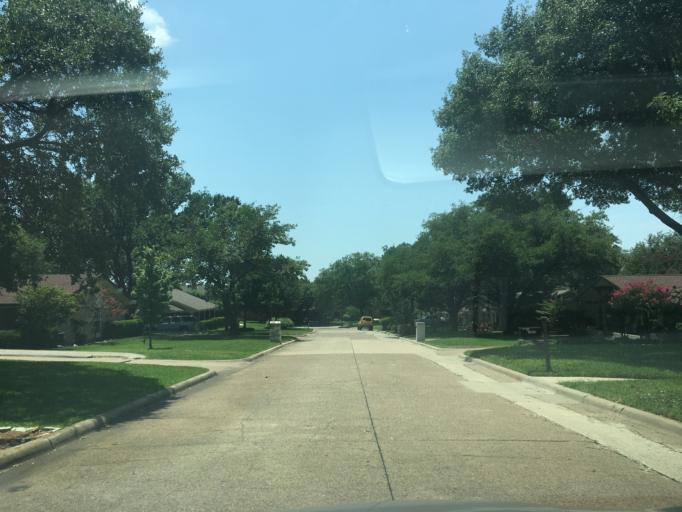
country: US
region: Texas
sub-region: Dallas County
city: Addison
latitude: 32.9454
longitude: -96.8571
